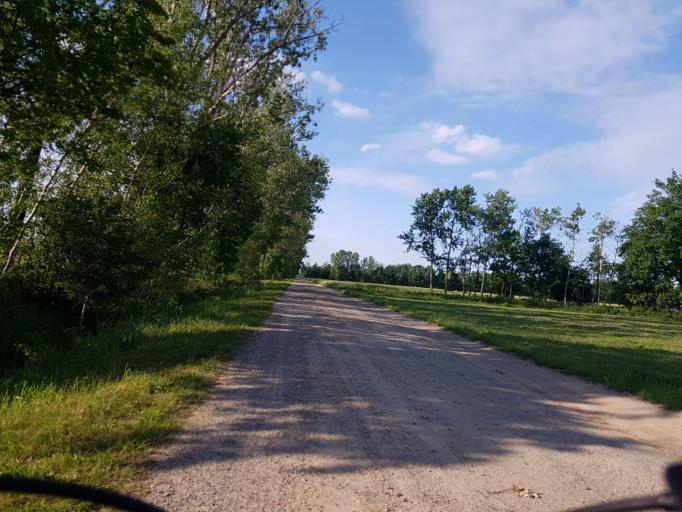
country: DE
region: Brandenburg
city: Merzdorf
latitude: 51.4300
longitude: 13.5287
